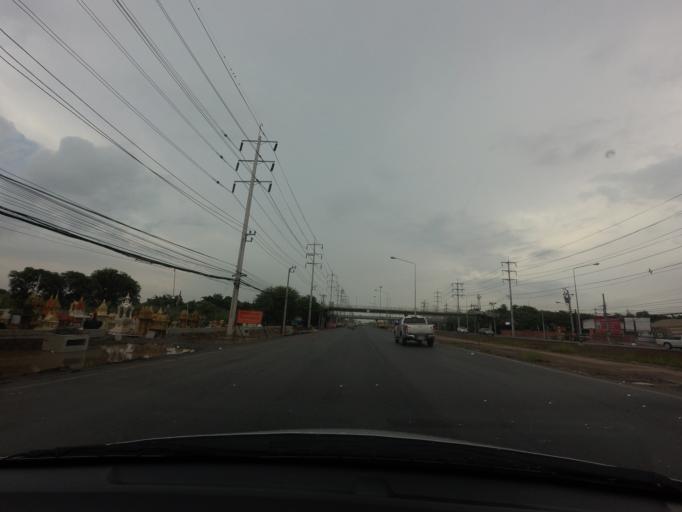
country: TH
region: Bangkok
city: Nong Chok
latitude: 13.8074
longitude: 100.8351
